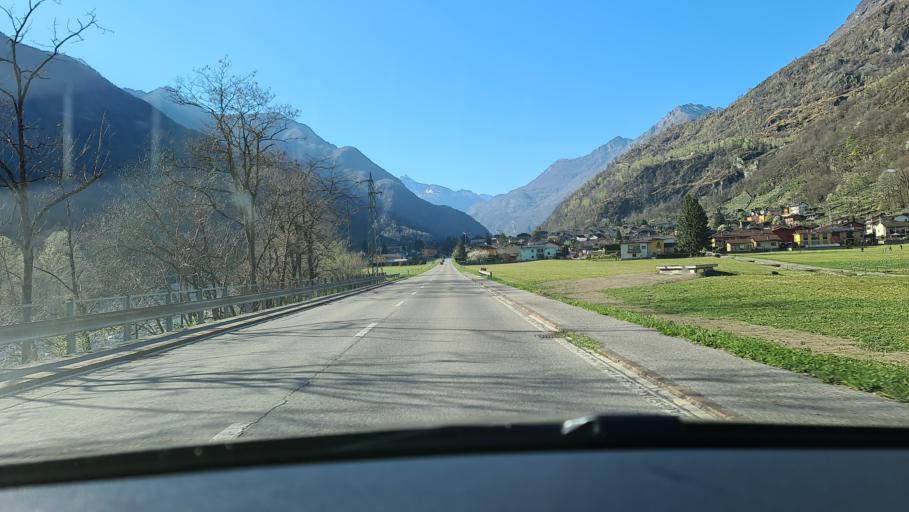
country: CH
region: Ticino
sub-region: Locarno District
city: Verscio
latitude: 46.2409
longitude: 8.7134
